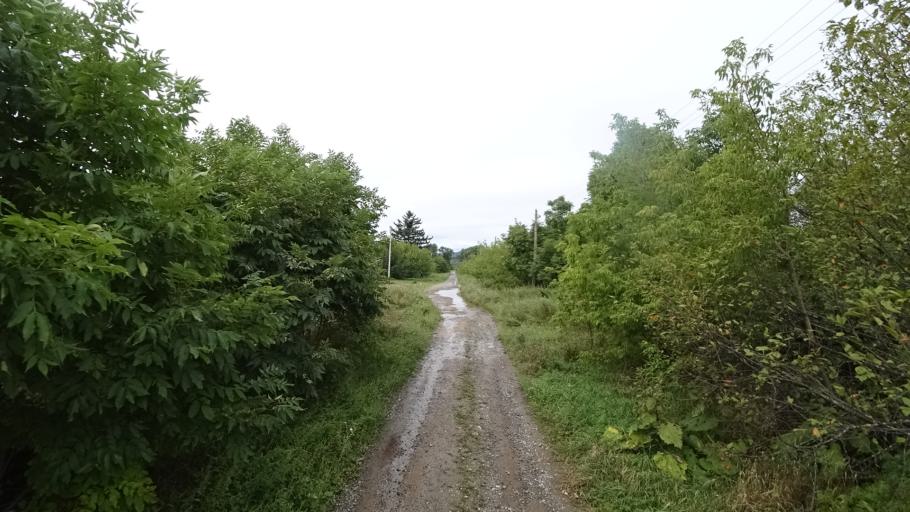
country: RU
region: Primorskiy
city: Lyalichi
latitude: 44.0779
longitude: 132.4825
